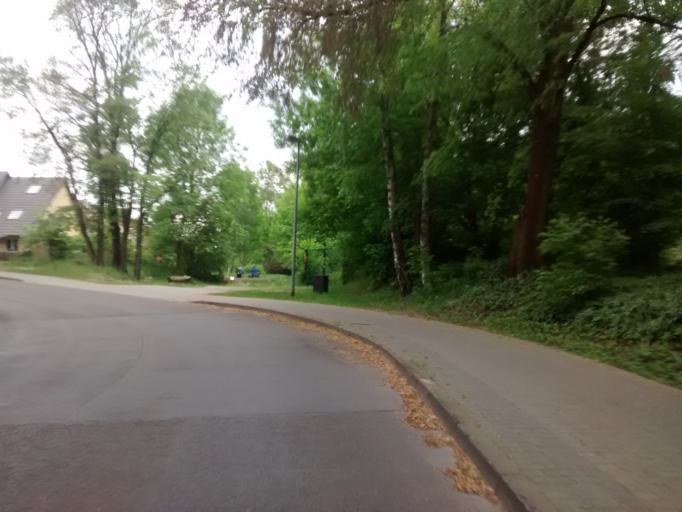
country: DE
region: Brandenburg
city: Hohen Neuendorf
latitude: 52.6694
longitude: 13.2621
